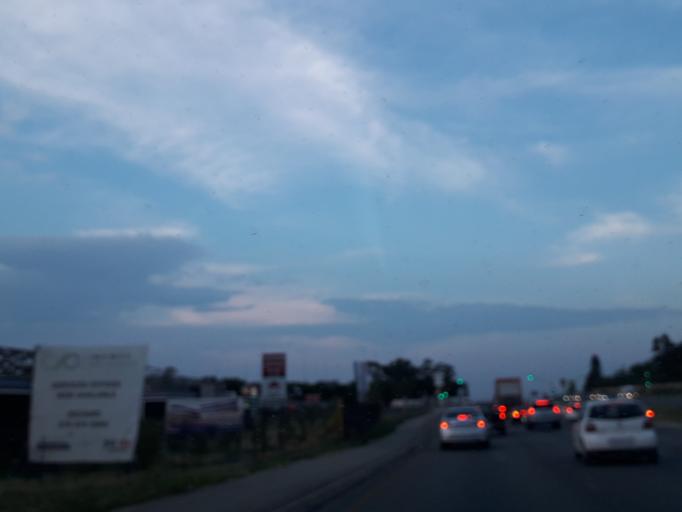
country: ZA
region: Gauteng
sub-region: City of Johannesburg Metropolitan Municipality
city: Diepsloot
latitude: -26.0045
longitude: 28.0126
